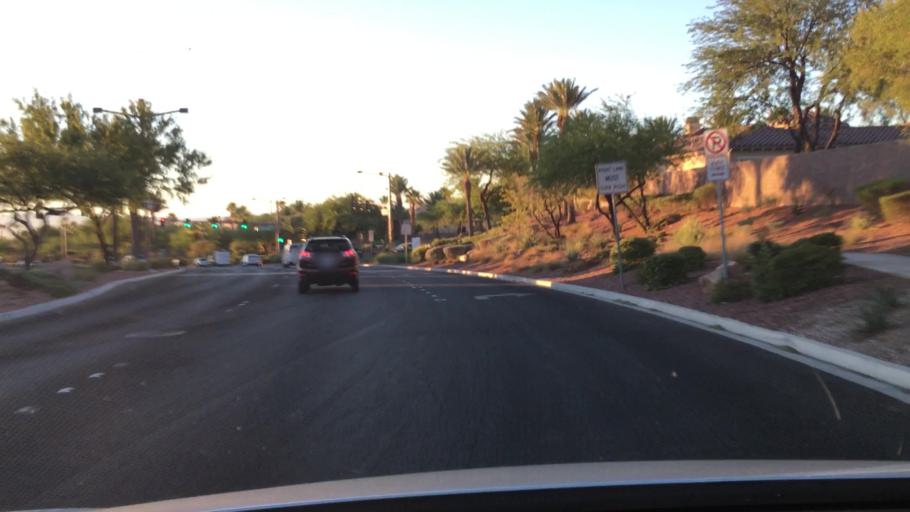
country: US
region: Nevada
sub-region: Clark County
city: Summerlin South
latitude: 36.1465
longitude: -115.3417
